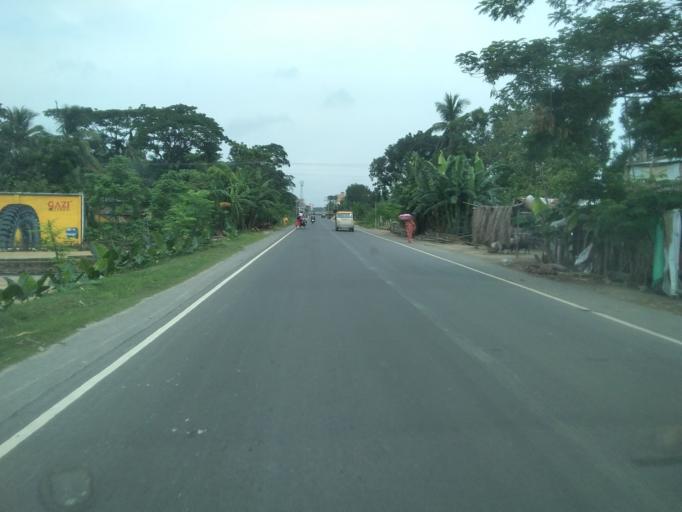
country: BD
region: Khulna
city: Kesabpur
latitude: 22.8377
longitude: 89.3015
